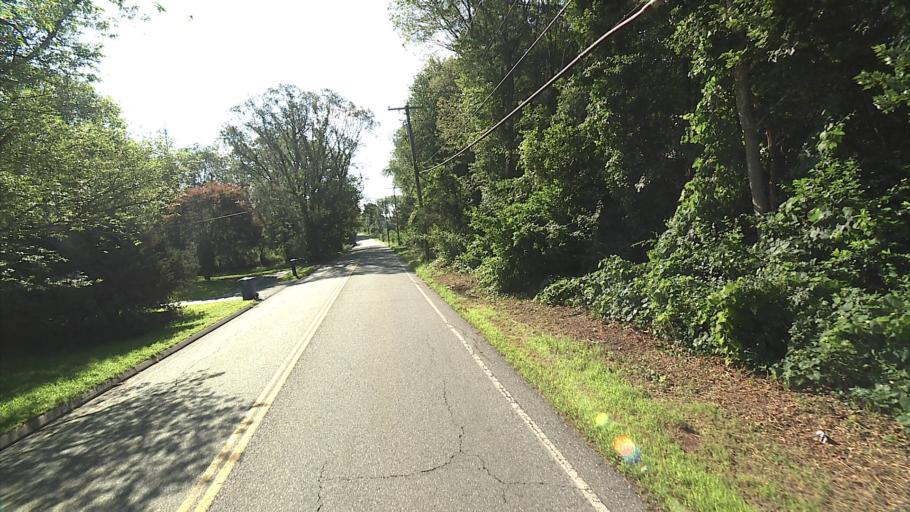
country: US
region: Connecticut
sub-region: New London County
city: Montville Center
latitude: 41.4940
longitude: -72.1818
